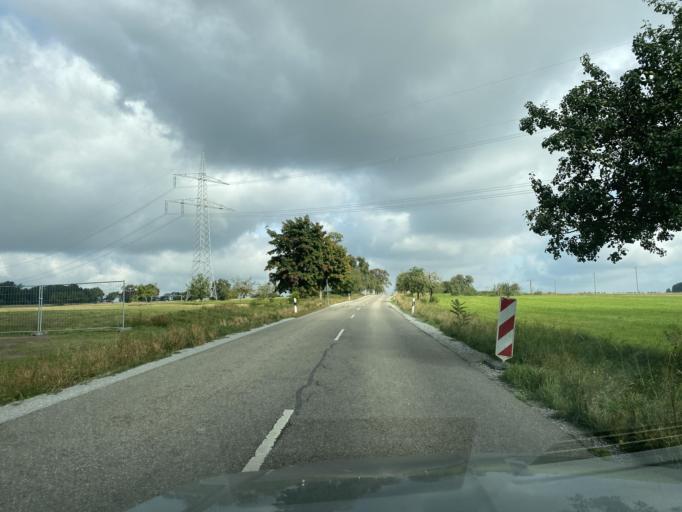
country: DE
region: Baden-Wuerttemberg
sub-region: Regierungsbezirk Stuttgart
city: Buhlertann
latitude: 49.0462
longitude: 9.9589
